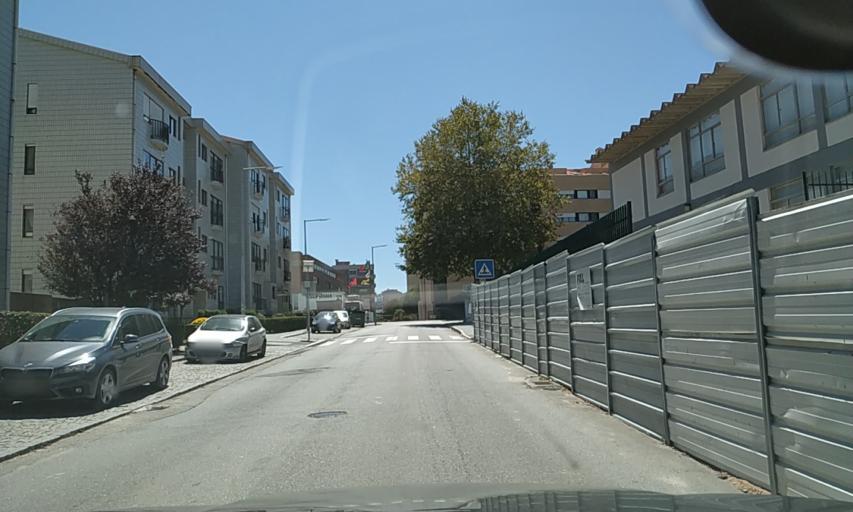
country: PT
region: Porto
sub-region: Vila Nova de Gaia
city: Canidelo
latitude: 41.1371
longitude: -8.6442
